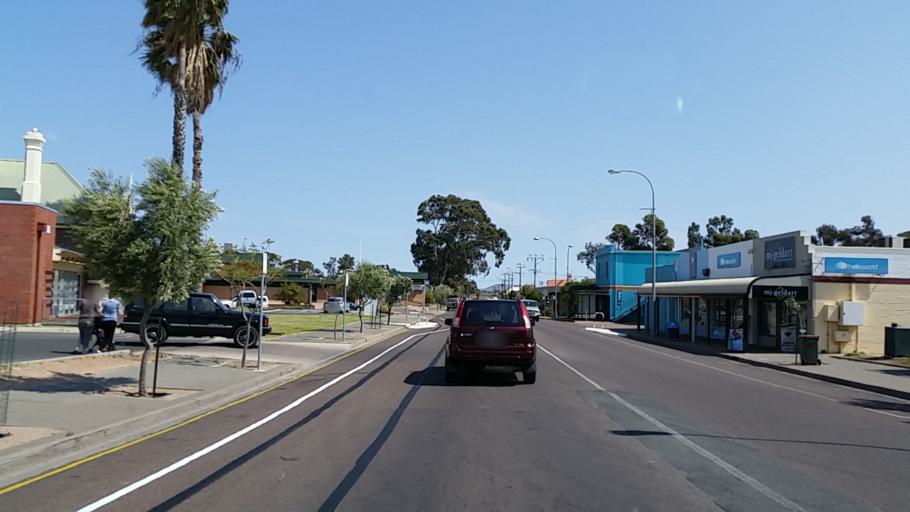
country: AU
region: South Australia
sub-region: Port Augusta
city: Port Augusta
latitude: -32.4932
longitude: 137.7647
